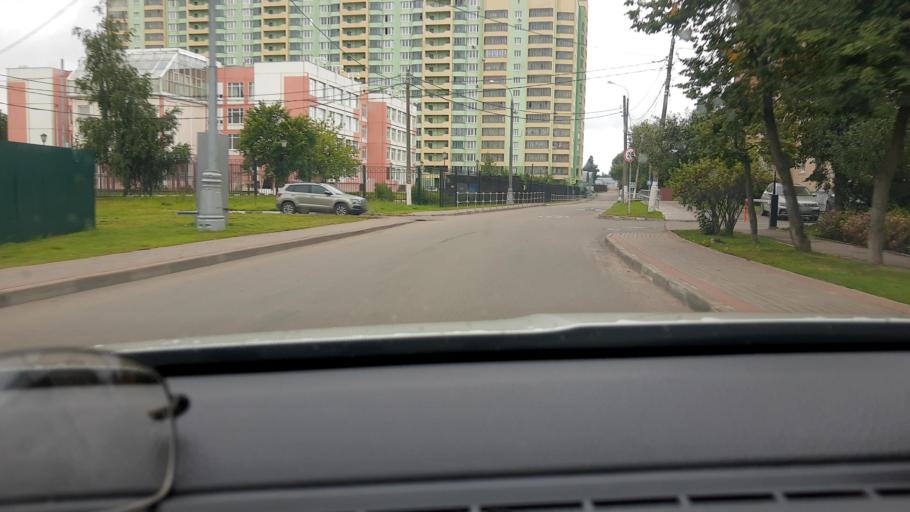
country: RU
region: Moscow
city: Vnukovo
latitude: 55.5944
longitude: 37.2073
